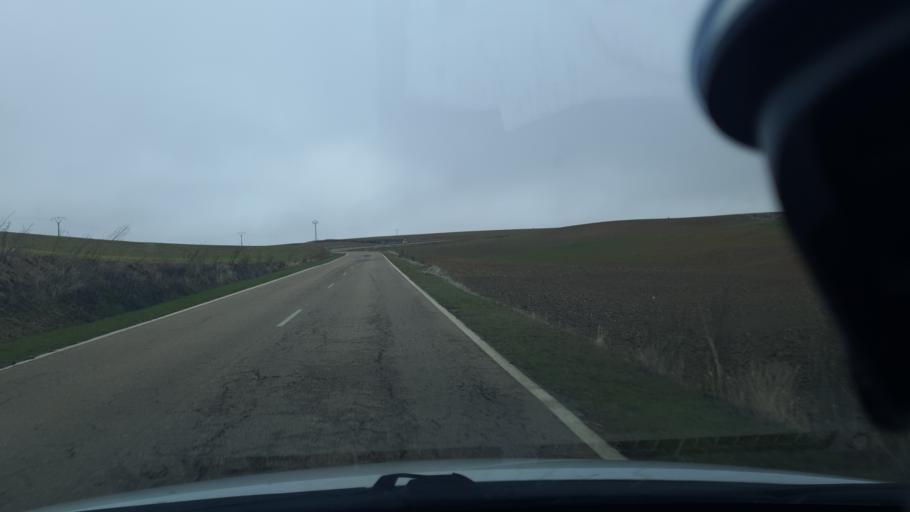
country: ES
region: Castille and Leon
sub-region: Provincia de Segovia
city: Hontanares de Eresma
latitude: 40.9897
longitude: -4.1992
